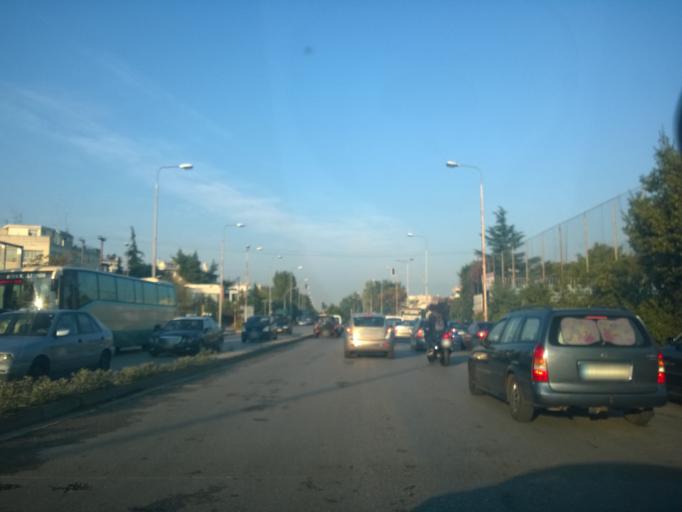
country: GR
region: Central Macedonia
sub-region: Nomos Thessalonikis
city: Evosmos
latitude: 40.6606
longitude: 22.9134
